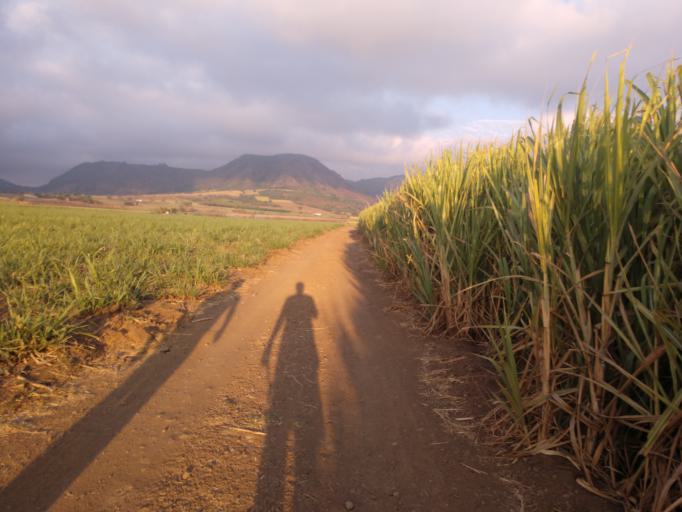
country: MX
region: Nayarit
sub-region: Tepic
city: La Corregidora
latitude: 21.4850
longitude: -104.8081
